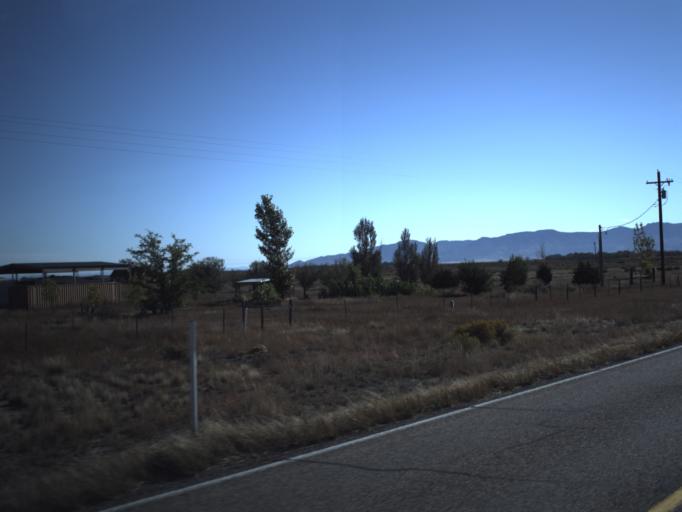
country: US
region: Utah
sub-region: Washington County
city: Enterprise
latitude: 37.7244
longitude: -113.6978
